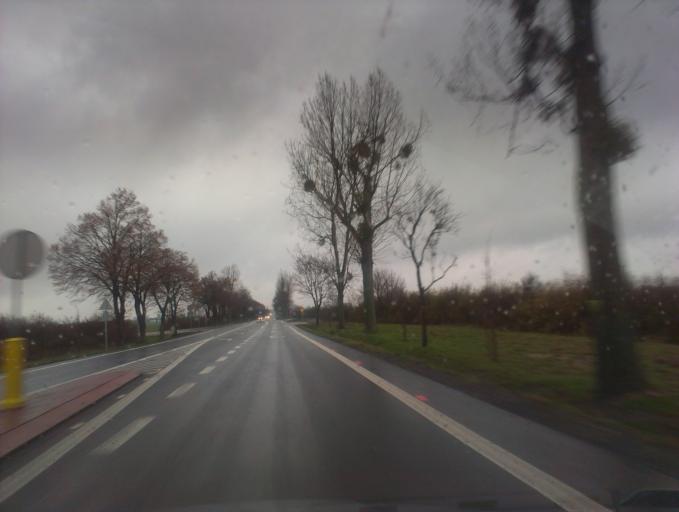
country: PL
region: Greater Poland Voivodeship
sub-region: Powiat obornicki
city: Oborniki
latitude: 52.6058
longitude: 16.8182
